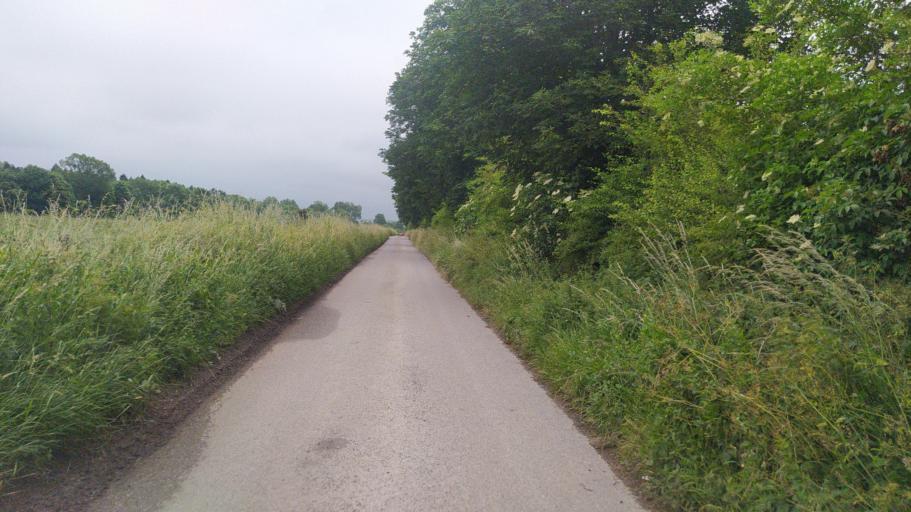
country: GB
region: England
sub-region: Wiltshire
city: Boyton
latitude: 51.1950
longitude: -2.1016
